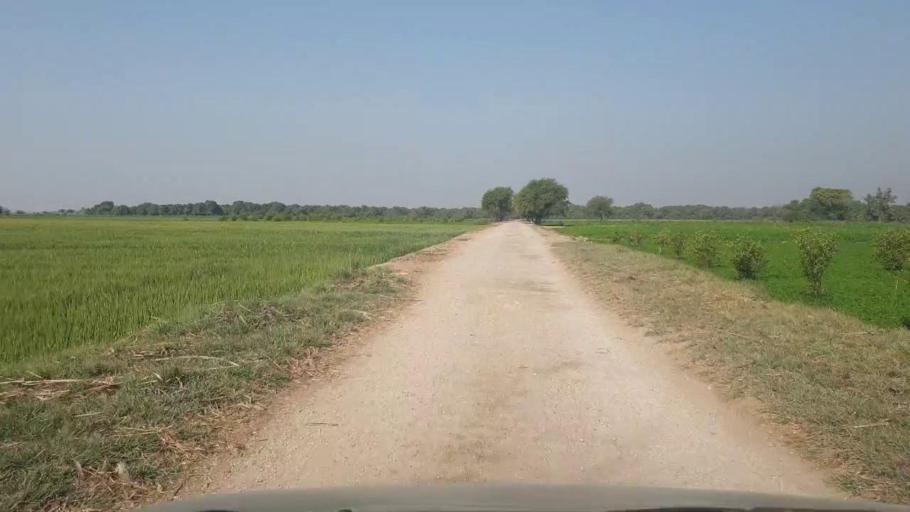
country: PK
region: Sindh
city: Mirwah Gorchani
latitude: 25.2554
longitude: 69.0947
